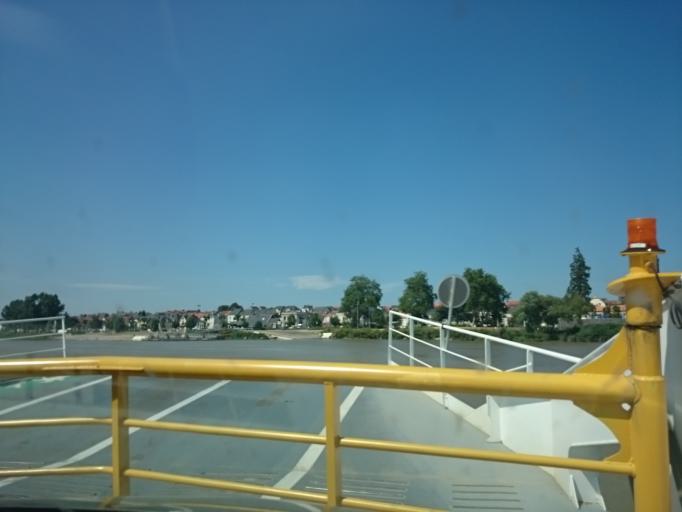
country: FR
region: Pays de la Loire
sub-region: Departement de la Loire-Atlantique
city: Indre
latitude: 47.1957
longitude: -1.6731
